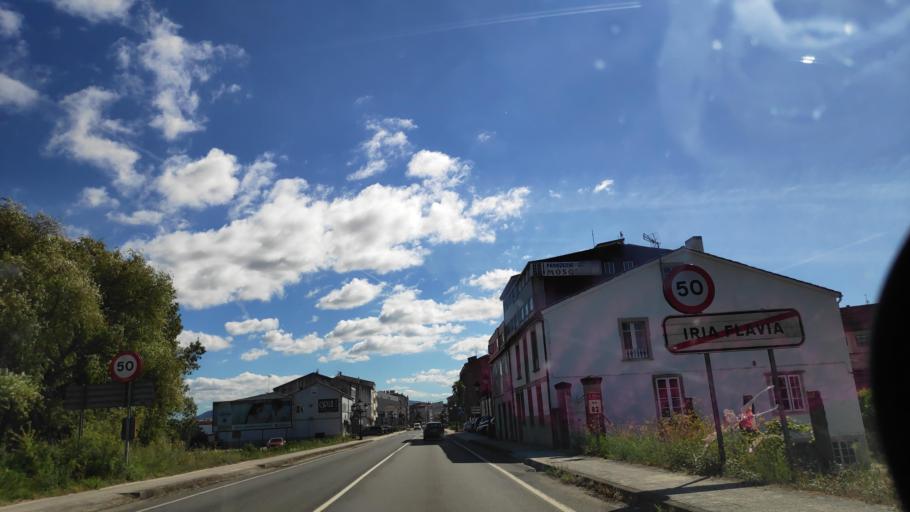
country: ES
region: Galicia
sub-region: Provincia da Coruna
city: Padron
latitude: 42.7445
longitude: -8.6565
